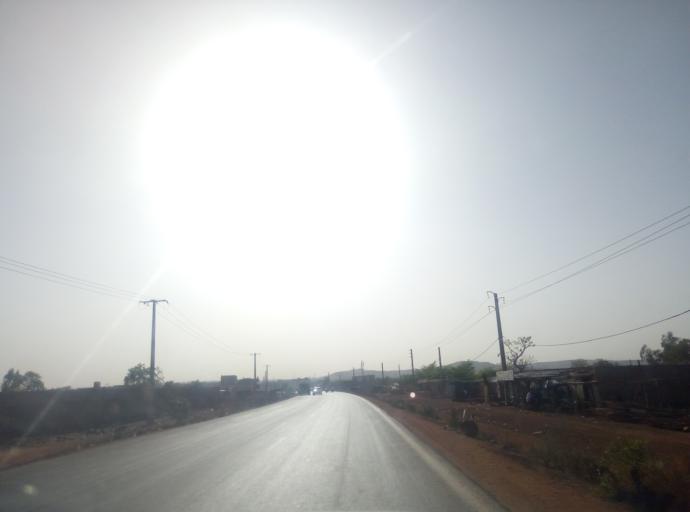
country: ML
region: Bamako
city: Bamako
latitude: 12.5866
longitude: -7.8303
